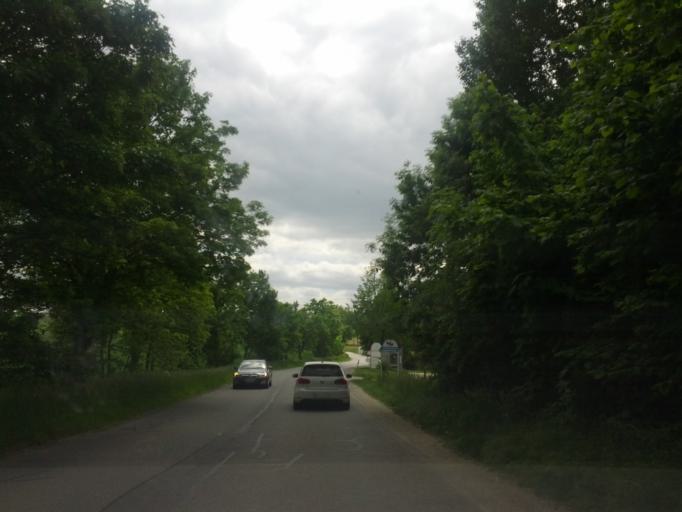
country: DE
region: Saxony
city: Bannewitz
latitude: 51.0019
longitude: 13.7640
